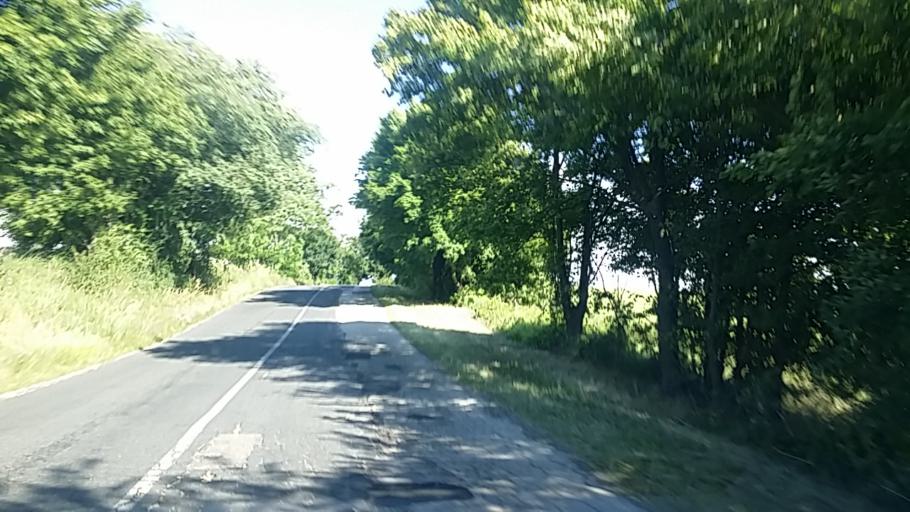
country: HU
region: Komarom-Esztergom
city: Tarjan
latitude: 47.6068
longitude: 18.5463
